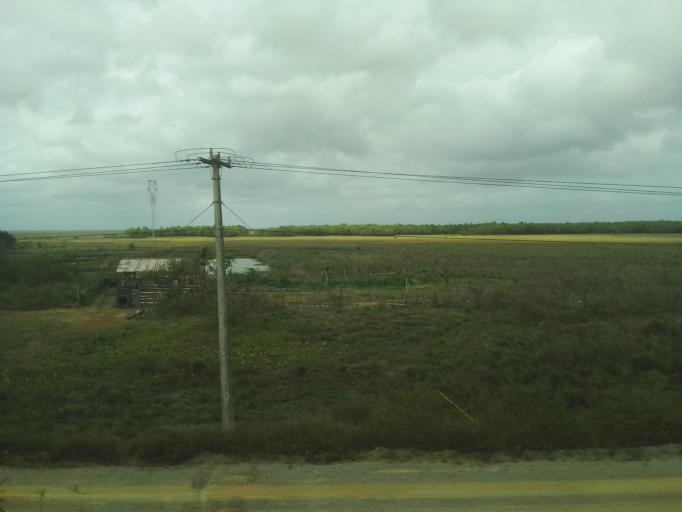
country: BR
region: Maranhao
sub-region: Icatu
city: Icatu
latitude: -2.9140
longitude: -44.3546
